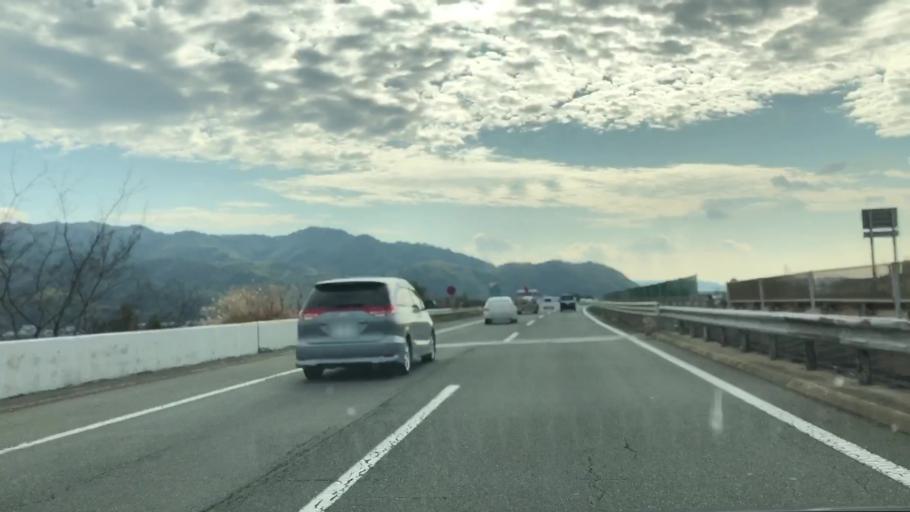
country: JP
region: Fukuoka
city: Setakamachi-takayanagi
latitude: 33.1802
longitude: 130.5178
